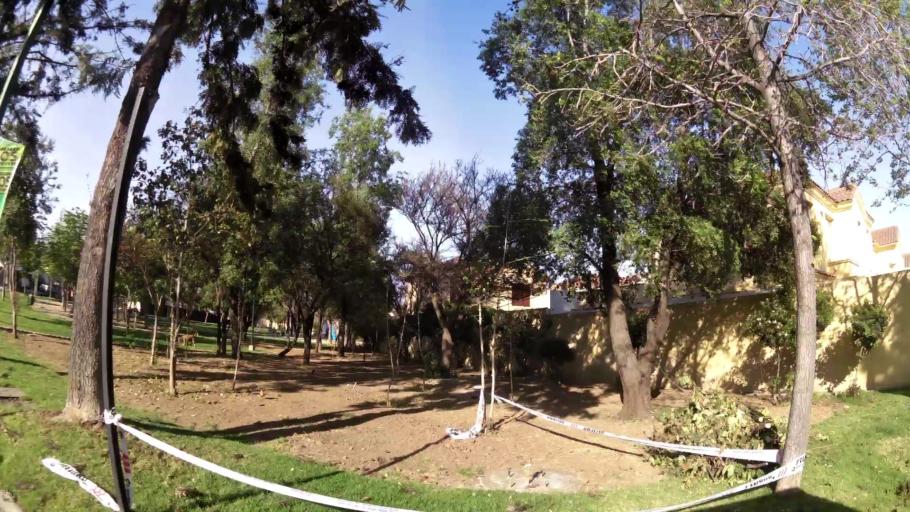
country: CL
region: Santiago Metropolitan
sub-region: Provincia de Santiago
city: Villa Presidente Frei, Nunoa, Santiago, Chile
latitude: -33.4850
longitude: -70.5547
